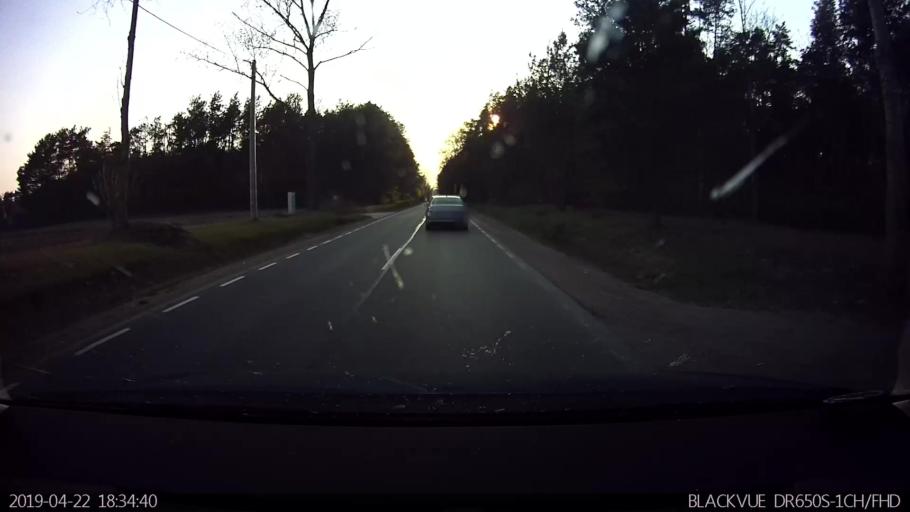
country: PL
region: Masovian Voivodeship
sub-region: Powiat wolominski
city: Klembow
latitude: 52.4455
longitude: 21.3645
